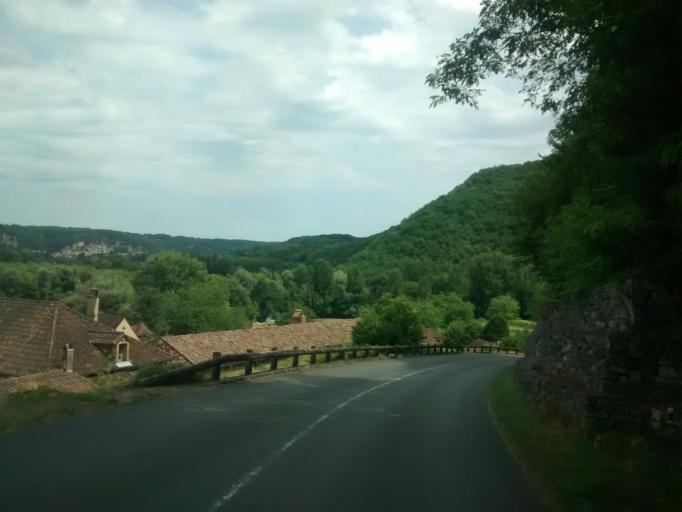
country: FR
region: Aquitaine
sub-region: Departement de la Dordogne
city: Cenac-et-Saint-Julien
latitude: 44.8135
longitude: 1.1503
